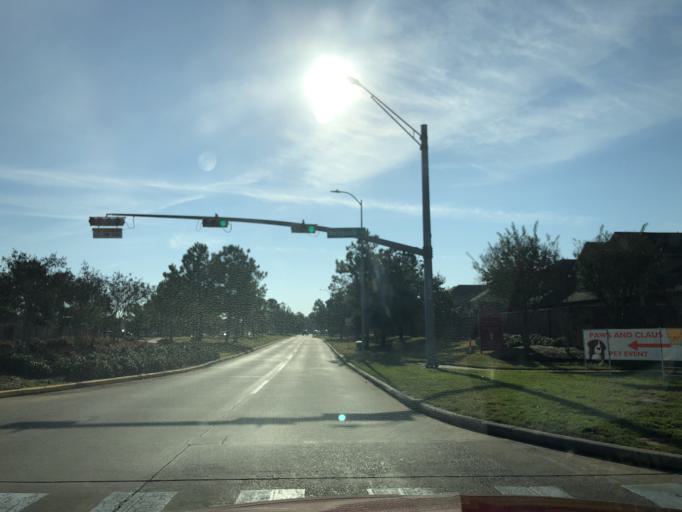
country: US
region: Texas
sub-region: Harris County
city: Tomball
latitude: 30.0498
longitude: -95.5661
